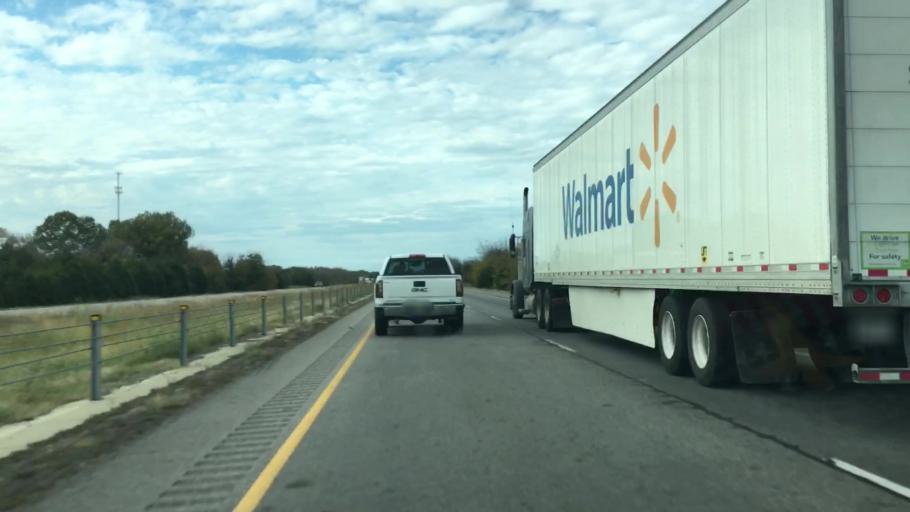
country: US
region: Arkansas
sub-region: Conway County
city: Morrilton
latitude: 35.2024
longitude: -92.8081
